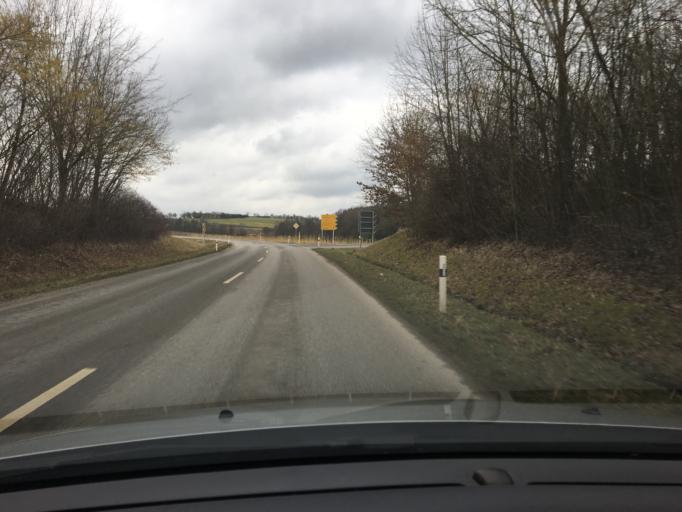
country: DE
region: Bavaria
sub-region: Lower Bavaria
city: Gangkofen
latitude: 48.4378
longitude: 12.5761
